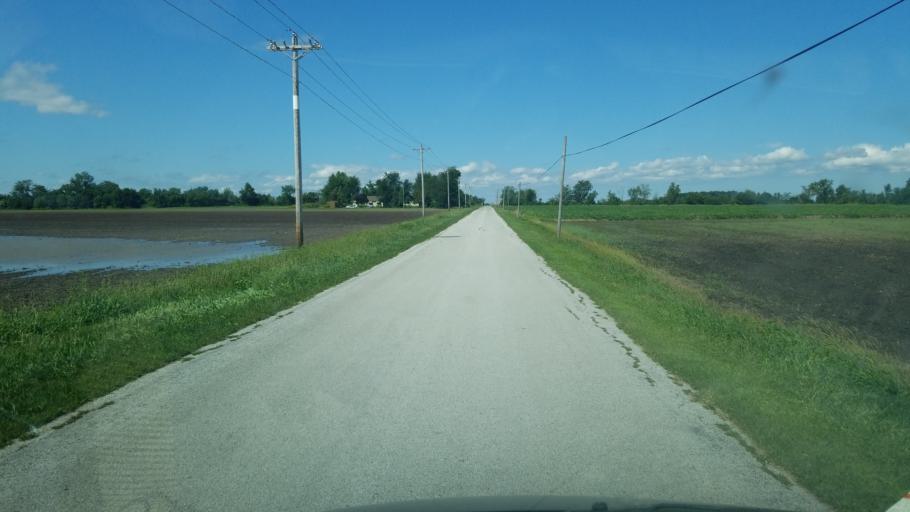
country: US
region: Ohio
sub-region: Henry County
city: Deshler
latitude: 41.2408
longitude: -83.8260
